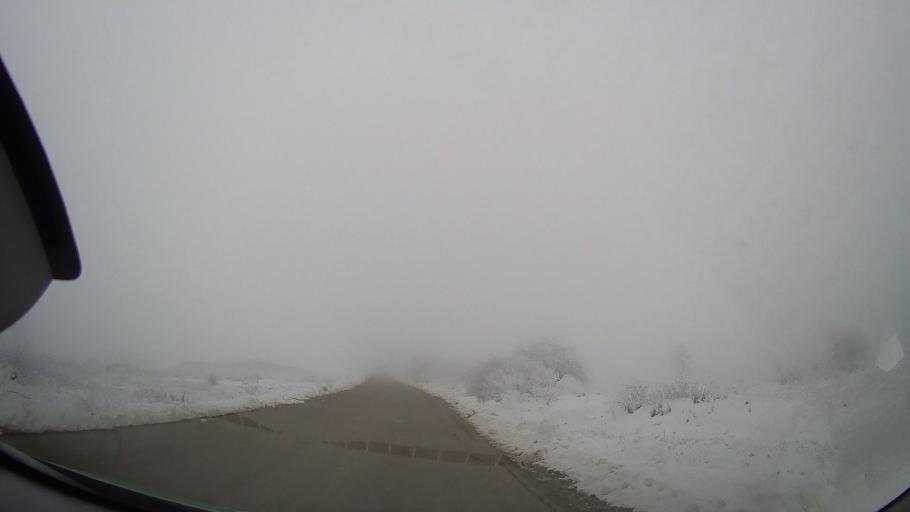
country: RO
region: Iasi
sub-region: Comuna Tansa
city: Suhulet
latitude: 46.8895
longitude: 27.2696
